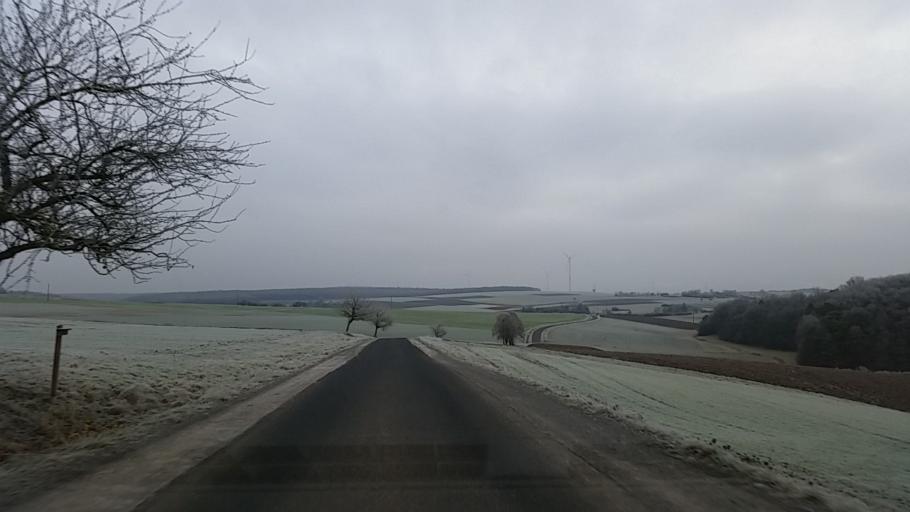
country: DE
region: Bavaria
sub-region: Regierungsbezirk Unterfranken
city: Fuchsstadt
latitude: 50.0427
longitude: 9.9114
